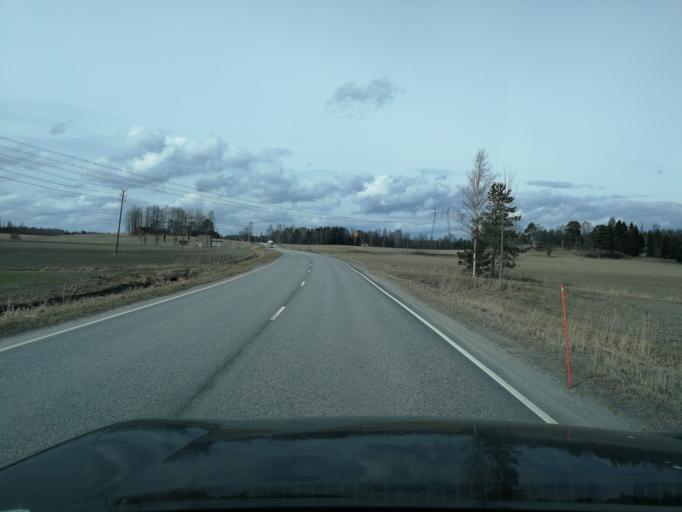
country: FI
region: Uusimaa
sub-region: Helsinki
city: Siuntio
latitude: 60.1186
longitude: 24.2408
